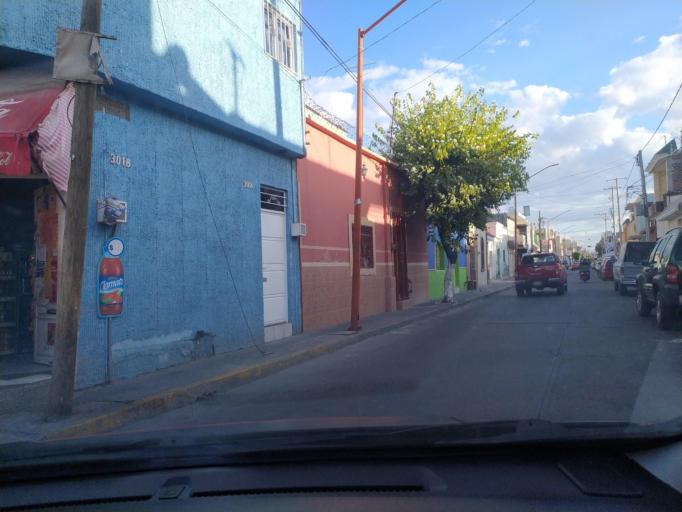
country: LA
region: Oudomxai
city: Muang La
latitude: 21.0176
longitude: 101.8536
